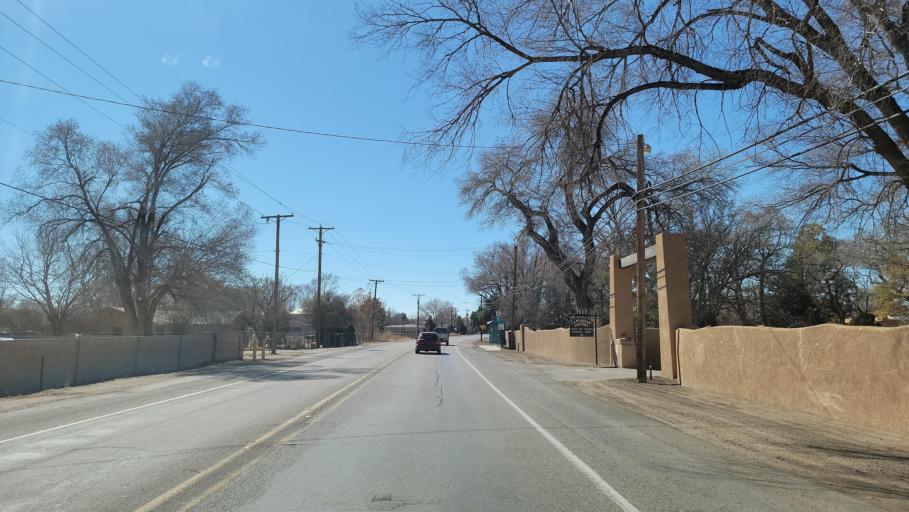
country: US
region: New Mexico
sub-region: Bernalillo County
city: South Valley
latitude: 35.0013
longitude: -106.6913
